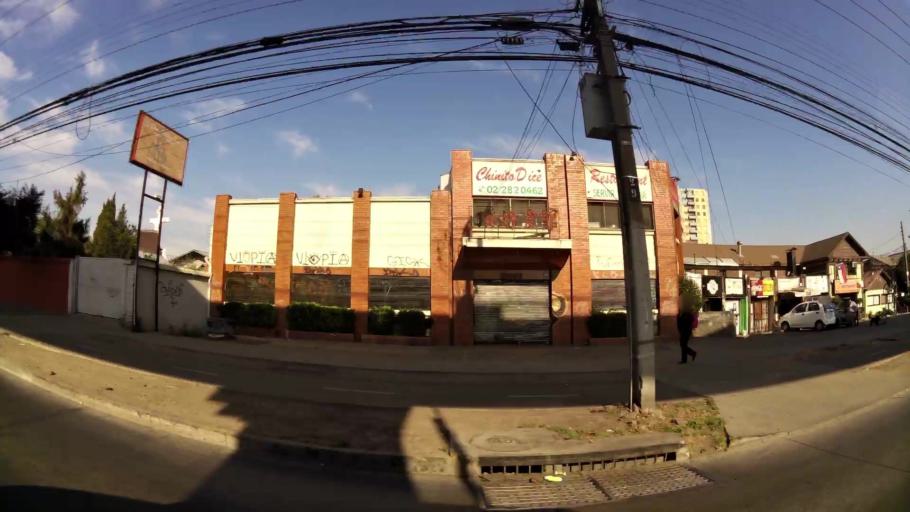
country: CL
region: Santiago Metropolitan
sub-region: Provincia de Santiago
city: La Pintana
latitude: -33.5518
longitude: -70.5870
